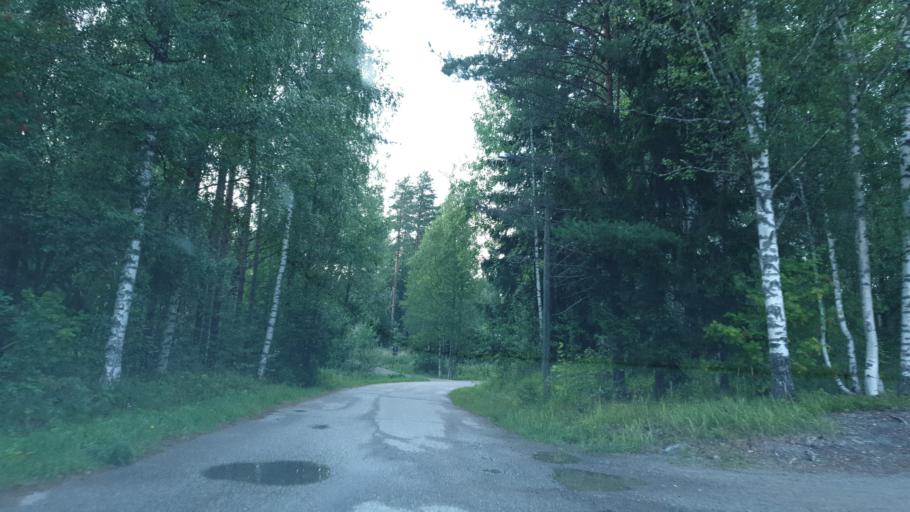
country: FI
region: Northern Savo
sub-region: Varkaus
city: Leppaevirta
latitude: 62.5879
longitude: 27.6072
